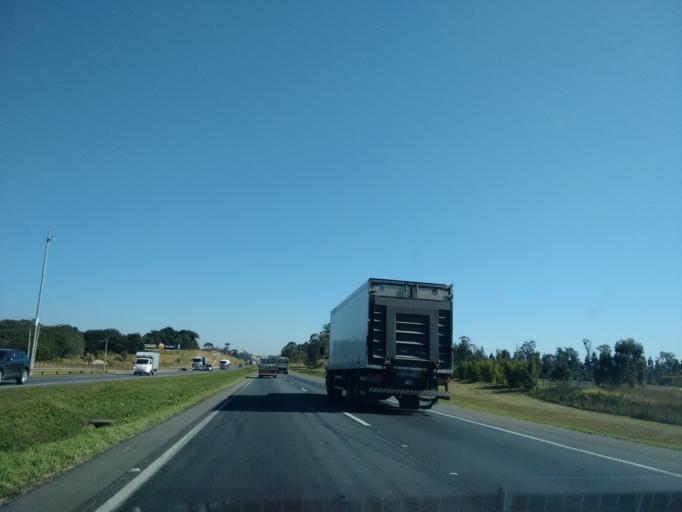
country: BR
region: Parana
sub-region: Sao Jose Dos Pinhais
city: Sao Jose dos Pinhais
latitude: -25.5658
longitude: -49.2442
